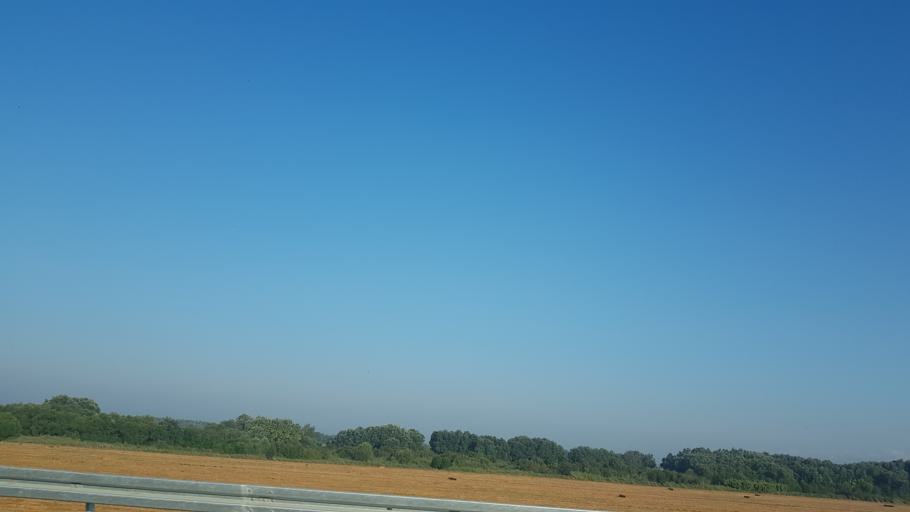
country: TR
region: Bursa
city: Karacabey
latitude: 40.1581
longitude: 28.3137
